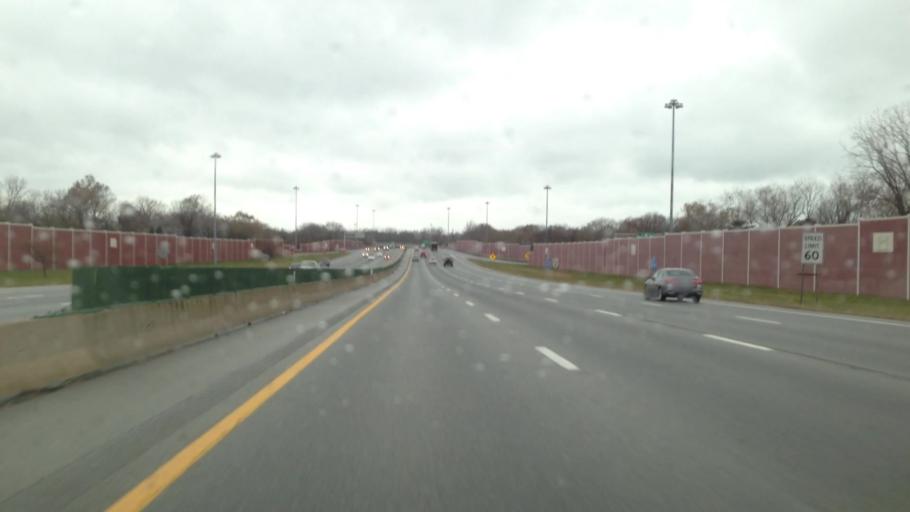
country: US
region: Ohio
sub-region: Cuyahoga County
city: East Cleveland
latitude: 41.5667
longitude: -81.5788
